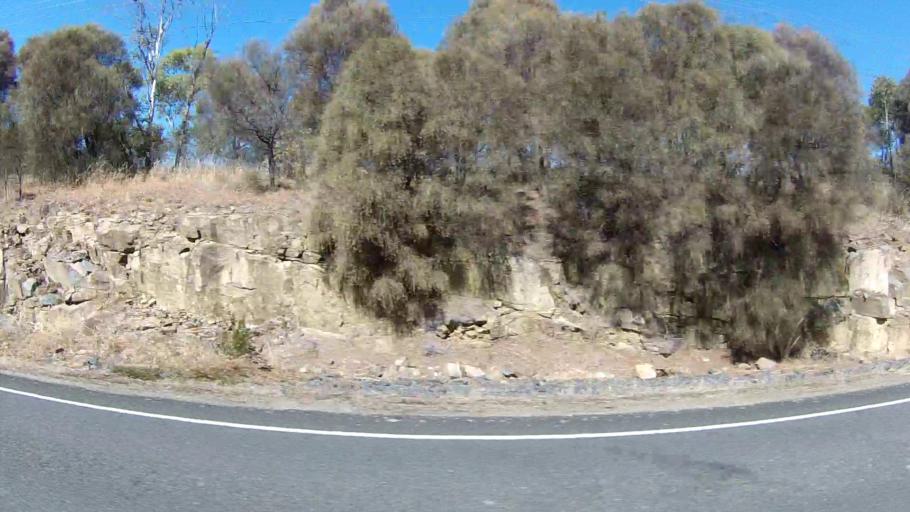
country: AU
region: Tasmania
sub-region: Sorell
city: Sorell
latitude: -42.5840
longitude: 147.8075
